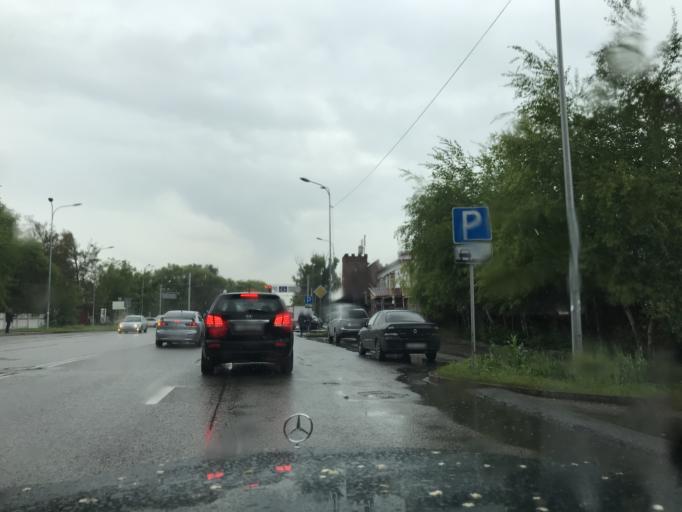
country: KZ
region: Almaty Oblysy
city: Pervomayskiy
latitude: 43.3457
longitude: 76.9683
